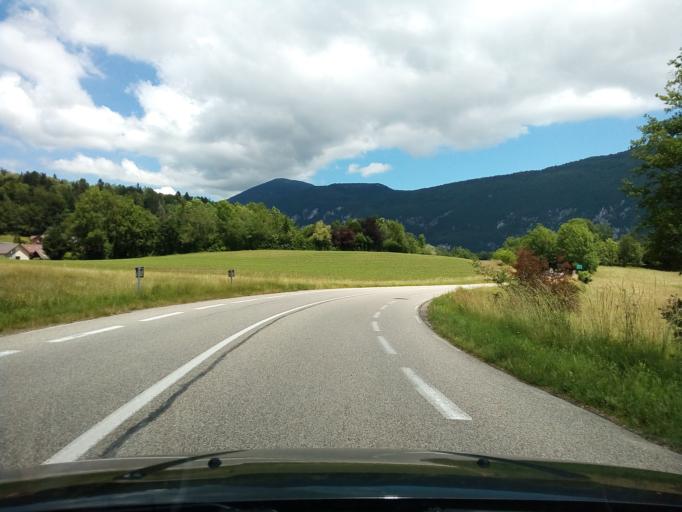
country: FR
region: Rhone-Alpes
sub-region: Departement de la Savoie
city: Novalaise
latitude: 45.5552
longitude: 5.7858
